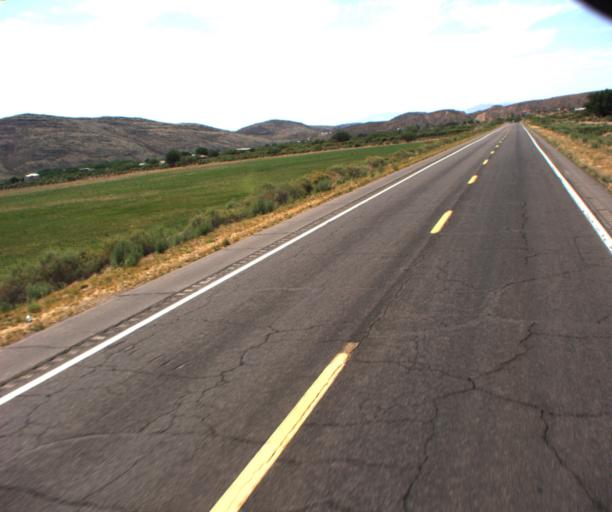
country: US
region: Arizona
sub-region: Greenlee County
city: Clifton
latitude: 32.8594
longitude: -109.1842
